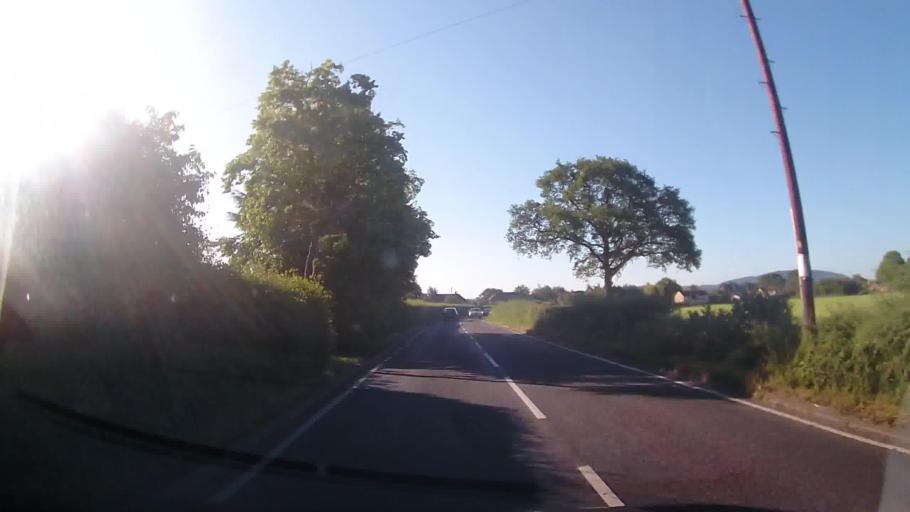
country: GB
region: England
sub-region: Shropshire
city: Withington
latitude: 52.7407
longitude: -2.5744
